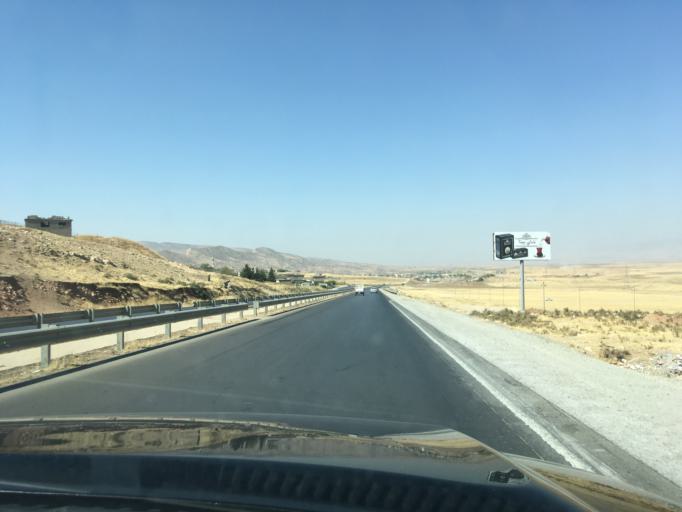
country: IQ
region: Arbil
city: Shaqlawah
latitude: 36.4908
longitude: 44.3757
